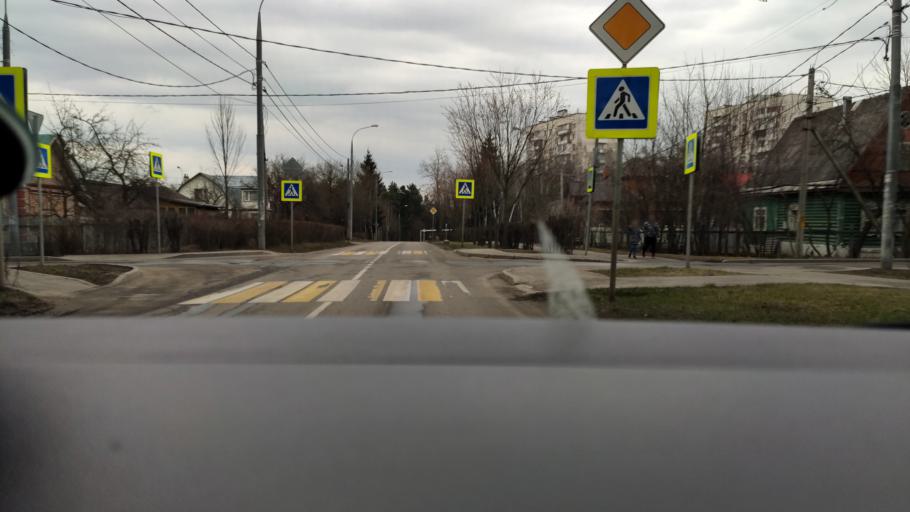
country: RU
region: Moskovskaya
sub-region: Leninskiy Rayon
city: Vnukovo
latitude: 55.6136
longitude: 37.3019
